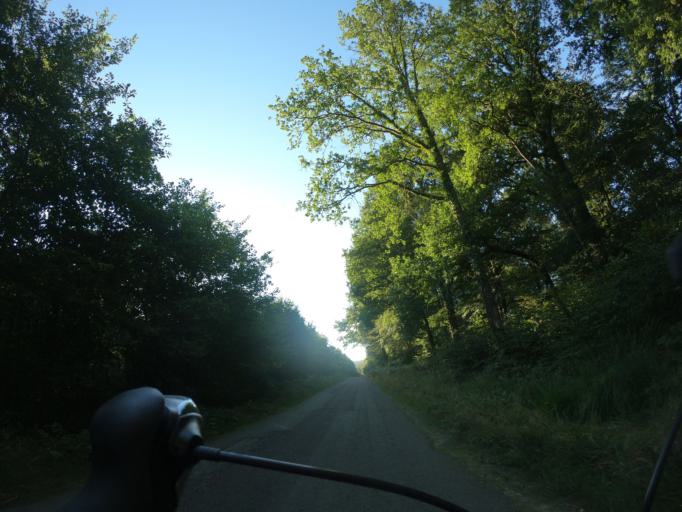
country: FR
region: Lower Normandy
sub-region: Departement de l'Orne
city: Magny-le-Desert
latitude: 48.5377
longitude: -0.3240
